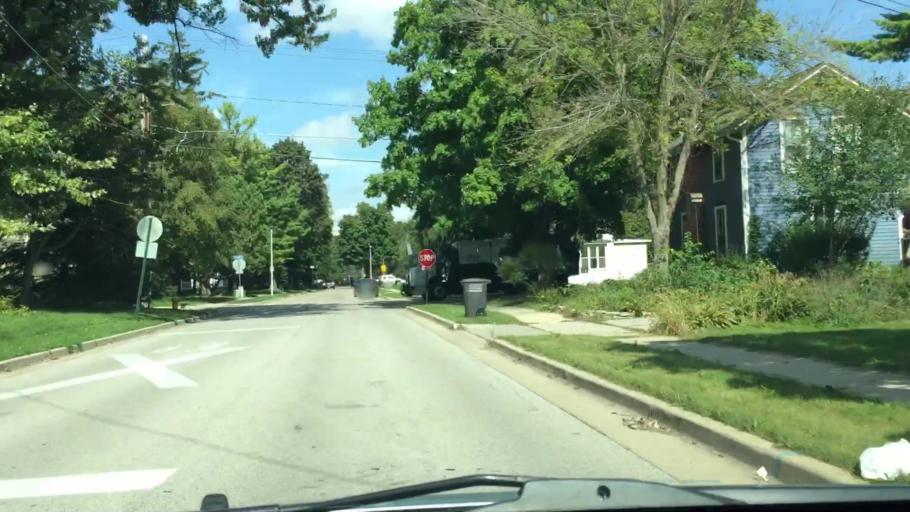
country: US
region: Wisconsin
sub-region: Waukesha County
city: Oconomowoc
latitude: 43.1125
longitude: -88.5128
